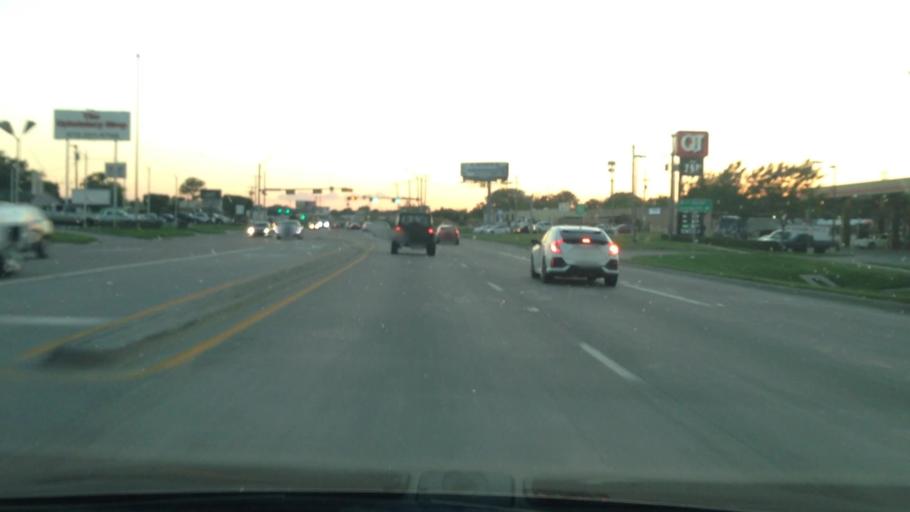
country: US
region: Texas
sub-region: Denton County
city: Lewisville
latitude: 33.0435
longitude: -96.9795
